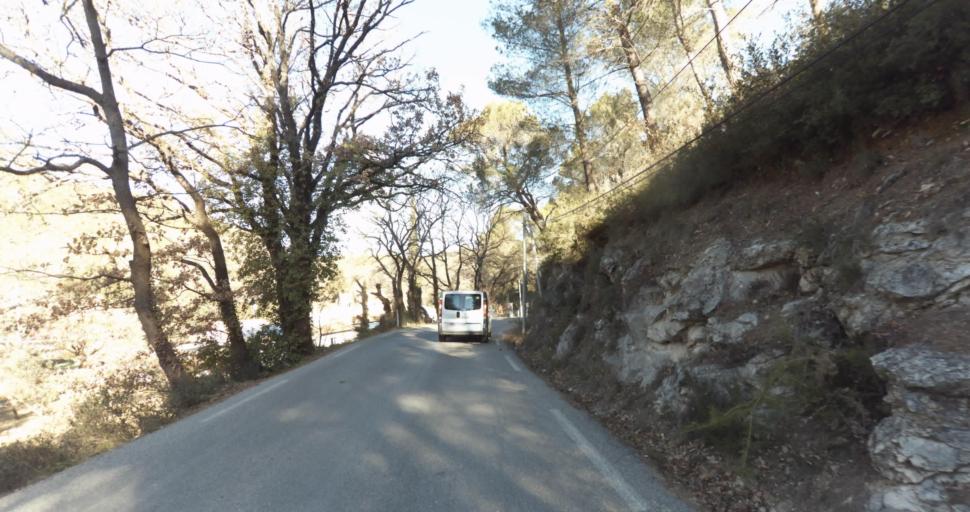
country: FR
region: Provence-Alpes-Cote d'Azur
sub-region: Departement des Bouches-du-Rhone
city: Peypin
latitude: 43.3680
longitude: 5.5645
